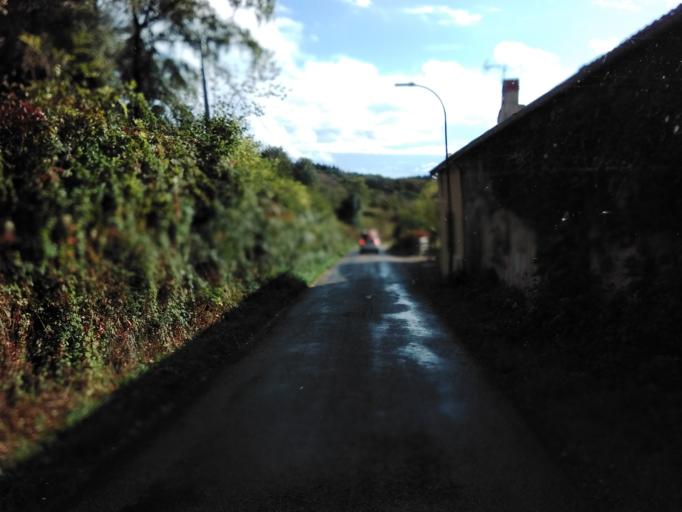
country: FR
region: Bourgogne
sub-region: Departement de la Nievre
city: Lormes
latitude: 47.2926
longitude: 3.8576
